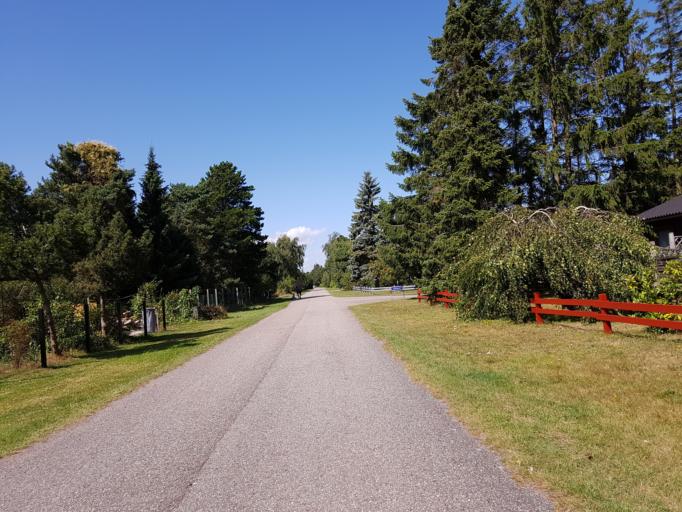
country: DK
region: Zealand
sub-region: Guldborgsund Kommune
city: Nykobing Falster
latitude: 54.5944
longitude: 11.9612
